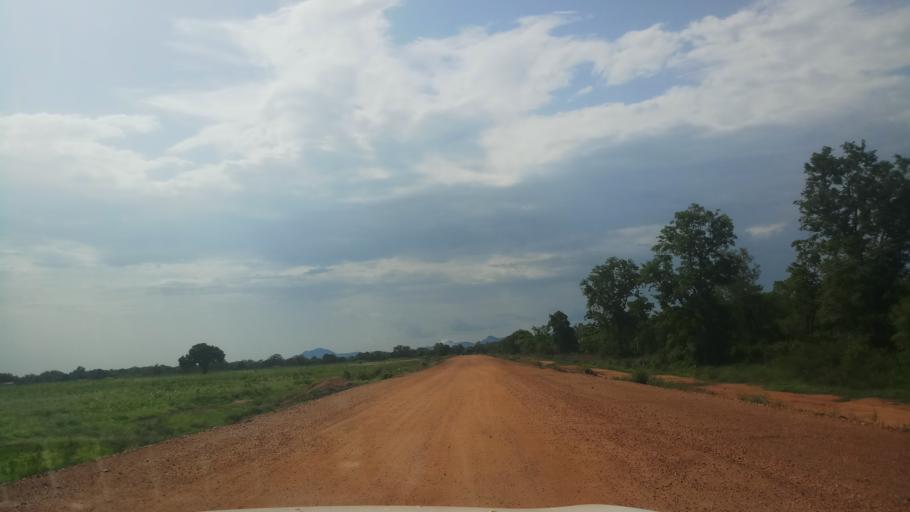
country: ET
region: Gambela
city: Gambela
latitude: 8.1581
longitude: 34.3356
